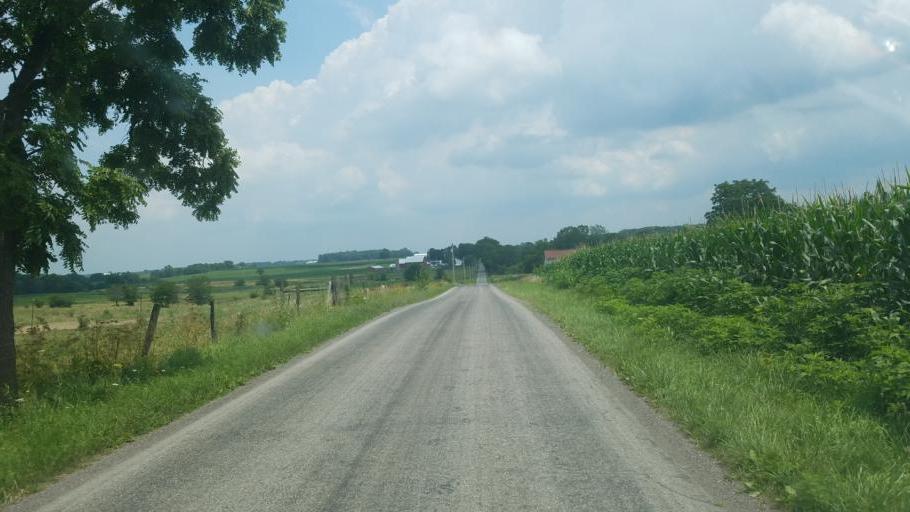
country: US
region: Ohio
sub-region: Hardin County
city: Kenton
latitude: 40.5930
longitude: -83.6266
